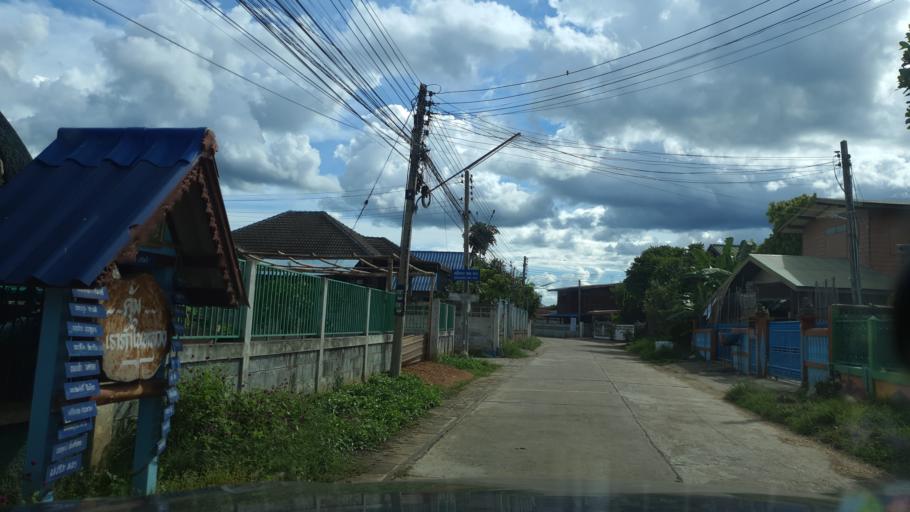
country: TH
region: Sukhothai
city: Thung Saliam
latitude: 17.3182
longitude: 99.5576
